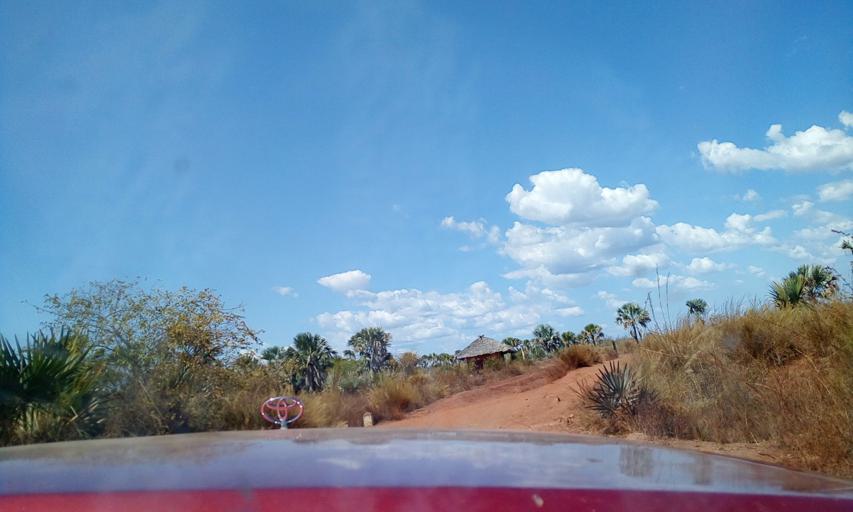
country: MG
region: Boeny
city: Sitampiky
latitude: -16.1179
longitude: 45.4704
